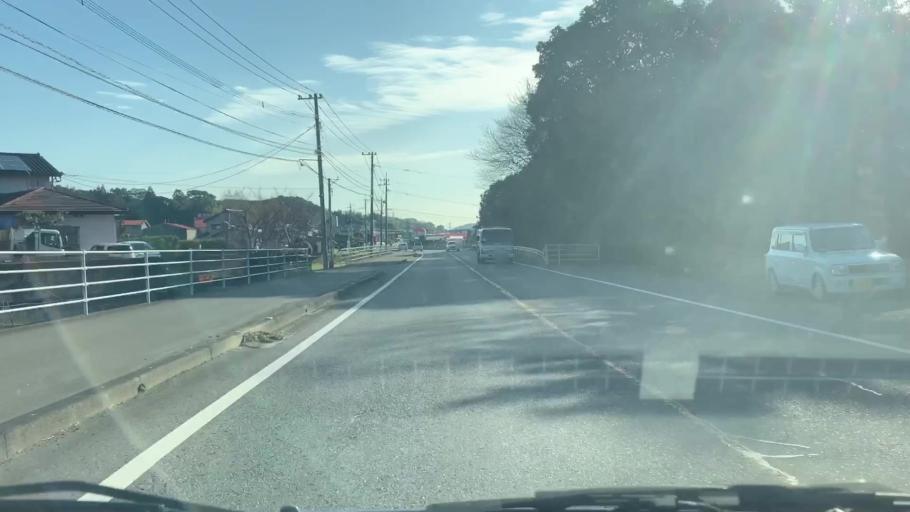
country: JP
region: Saga Prefecture
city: Takeocho-takeo
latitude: 33.2262
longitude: 130.0400
